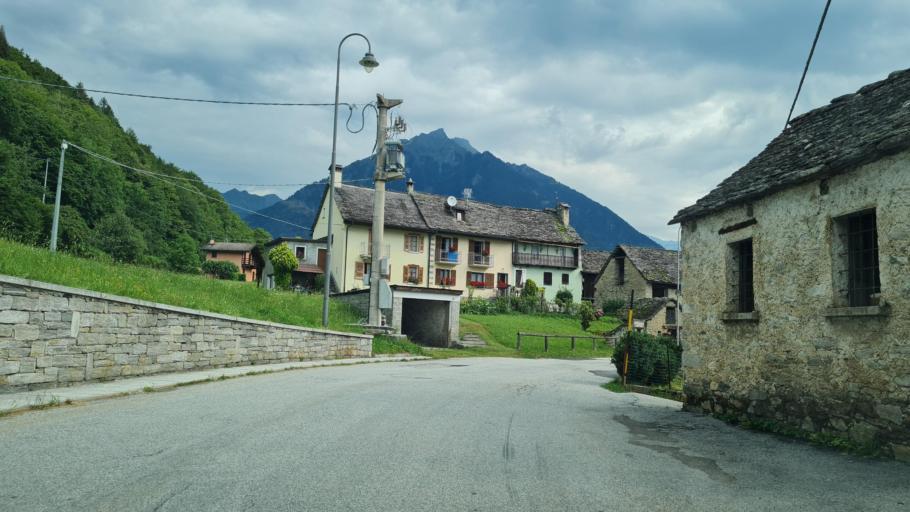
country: IT
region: Piedmont
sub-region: Provincia Verbano-Cusio-Ossola
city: Baceno
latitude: 46.2410
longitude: 8.3130
